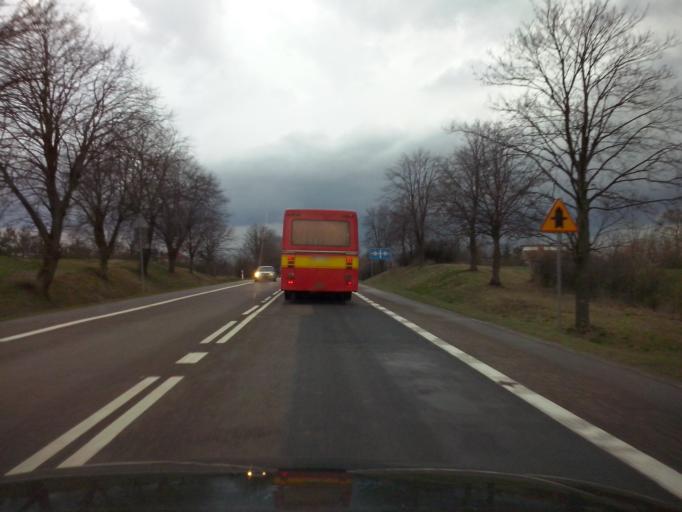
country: PL
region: Lublin Voivodeship
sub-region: Powiat chelmski
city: Rejowiec Fabryczny
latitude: 51.1739
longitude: 23.2714
